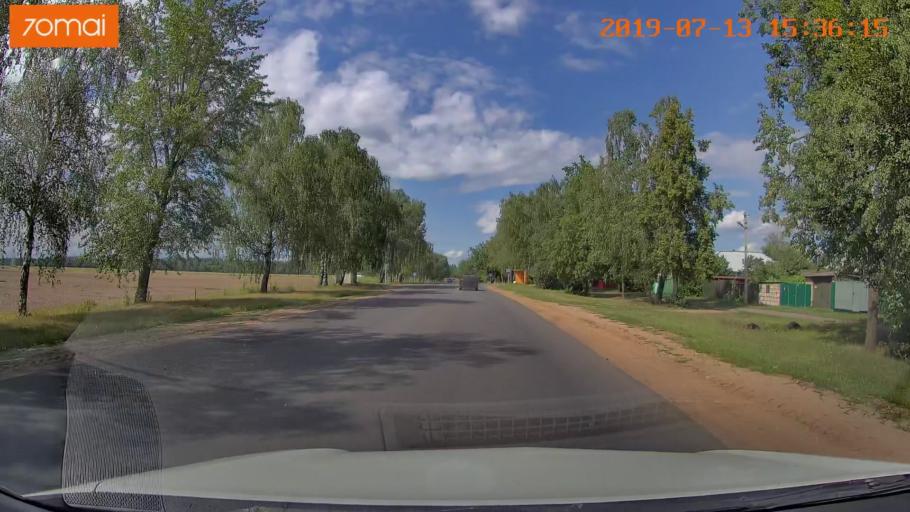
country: BY
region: Mogilev
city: Babruysk
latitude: 53.1298
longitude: 29.1668
